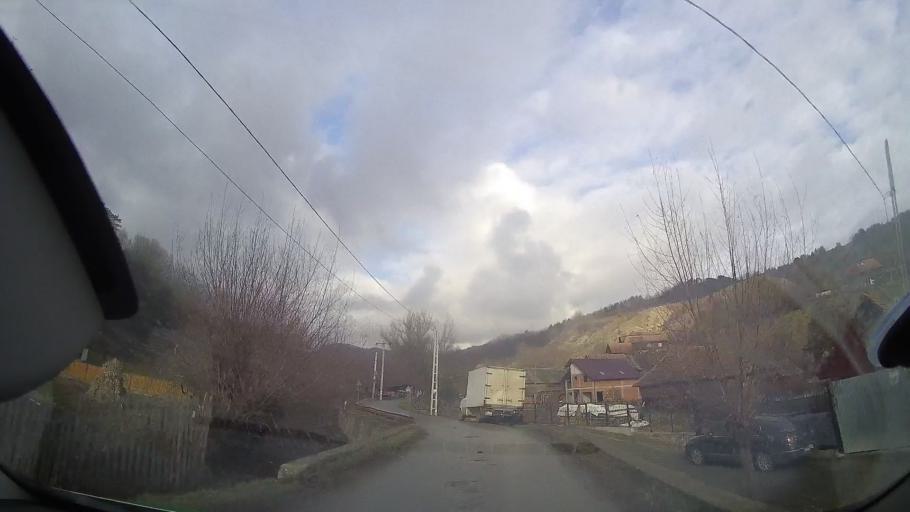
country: RO
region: Alba
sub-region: Comuna Ocolis
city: Ocolis
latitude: 46.4802
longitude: 23.4642
